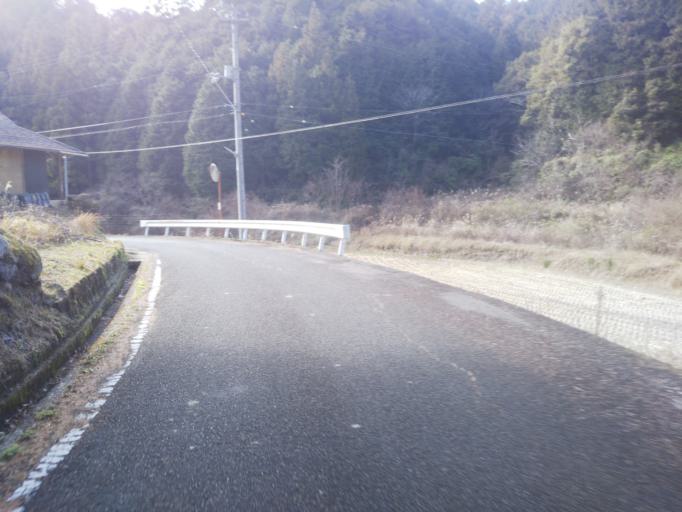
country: JP
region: Kochi
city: Nakamura
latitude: 33.0426
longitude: 132.9854
